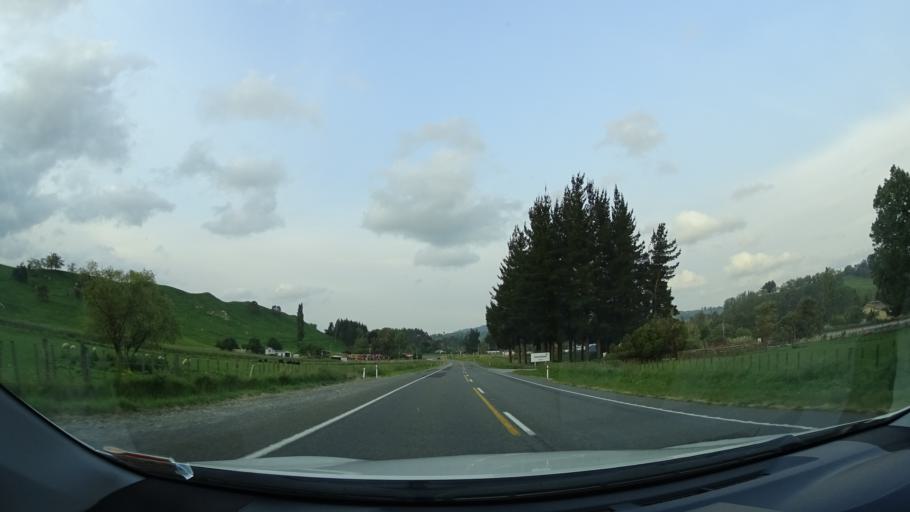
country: NZ
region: Manawatu-Wanganui
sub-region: Ruapehu District
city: Waiouru
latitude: -39.7362
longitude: 175.8415
